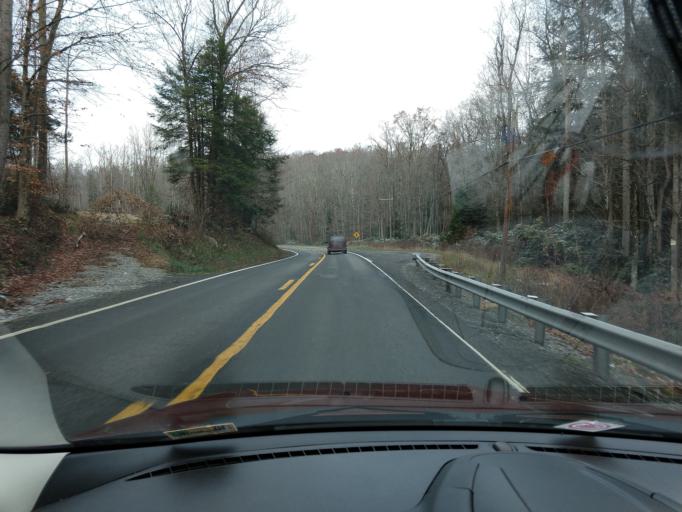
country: US
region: West Virginia
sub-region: Nicholas County
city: Craigsville
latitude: 38.2615
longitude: -80.7325
